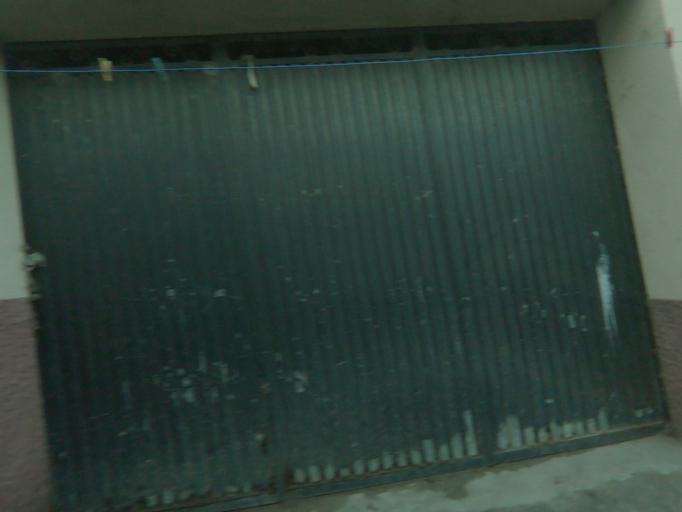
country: PT
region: Vila Real
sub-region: Peso da Regua
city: Godim
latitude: 41.1614
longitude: -7.8038
